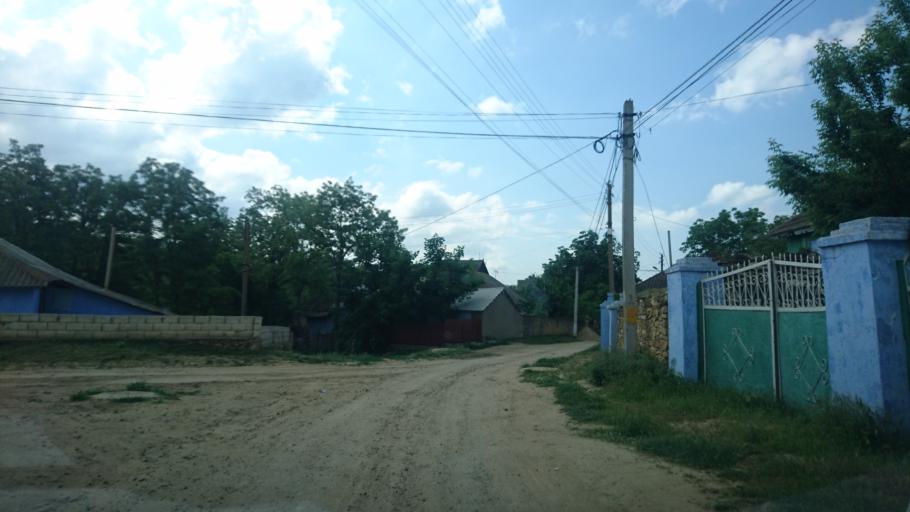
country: MD
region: Telenesti
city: Cocieri
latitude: 47.3604
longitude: 29.1035
